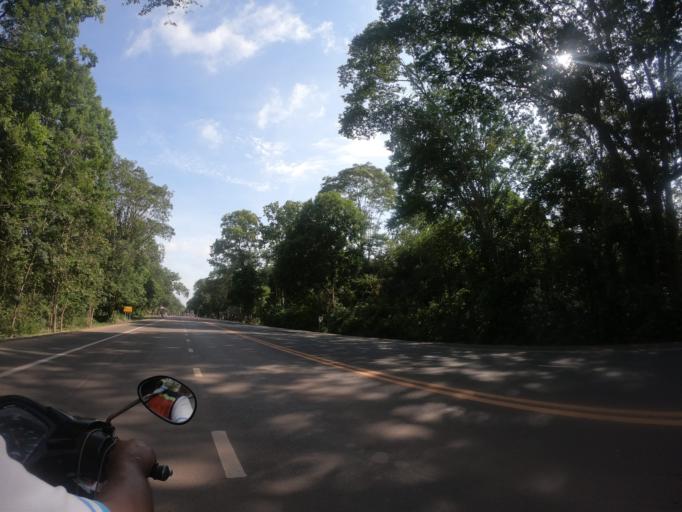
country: TH
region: Surin
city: Kap Choeng
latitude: 14.4394
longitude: 103.7007
